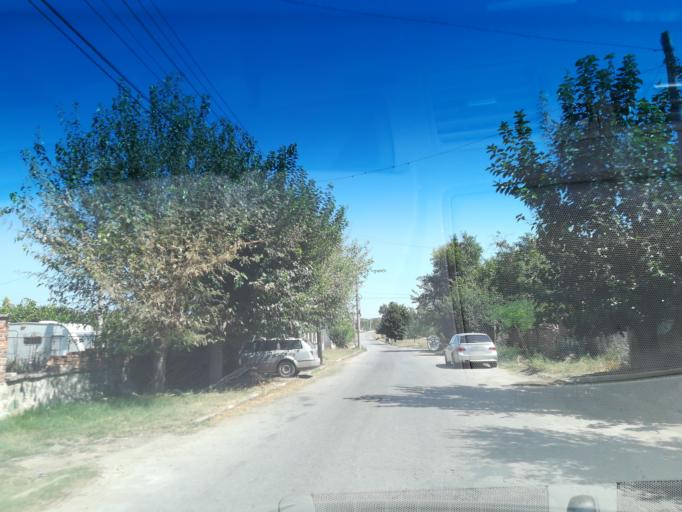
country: BG
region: Pazardzhik
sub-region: Obshtina Pazardzhik
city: Pazardzhik
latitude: 42.2515
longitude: 24.4355
